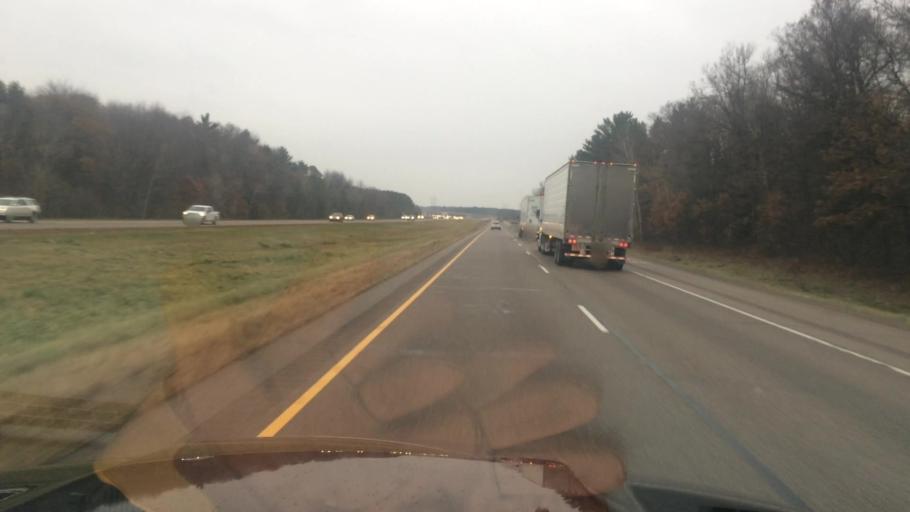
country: US
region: Wisconsin
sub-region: Portage County
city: Stevens Point
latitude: 44.5821
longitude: -89.6065
